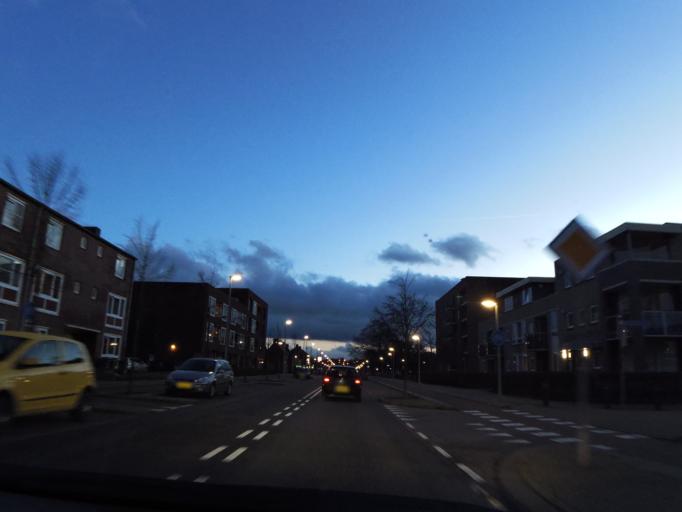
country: NL
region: Limburg
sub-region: Gemeente Roermond
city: Roermond
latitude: 51.1777
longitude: 6.0026
